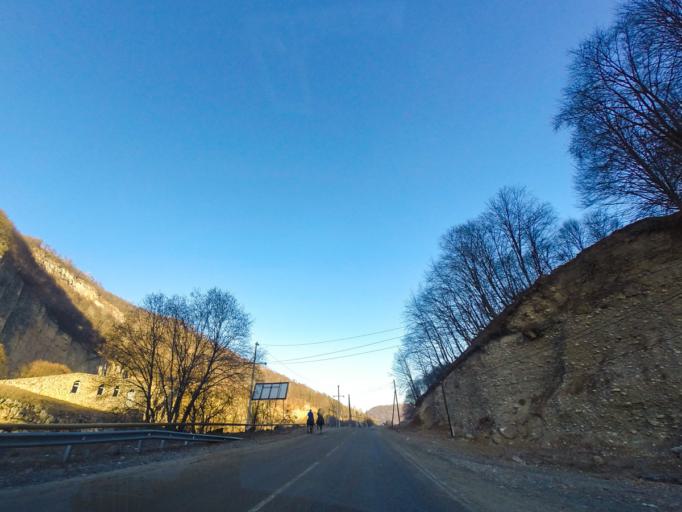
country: RU
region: Kabardino-Balkariya
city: Zhankhoteko
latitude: 43.4711
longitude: 43.2669
